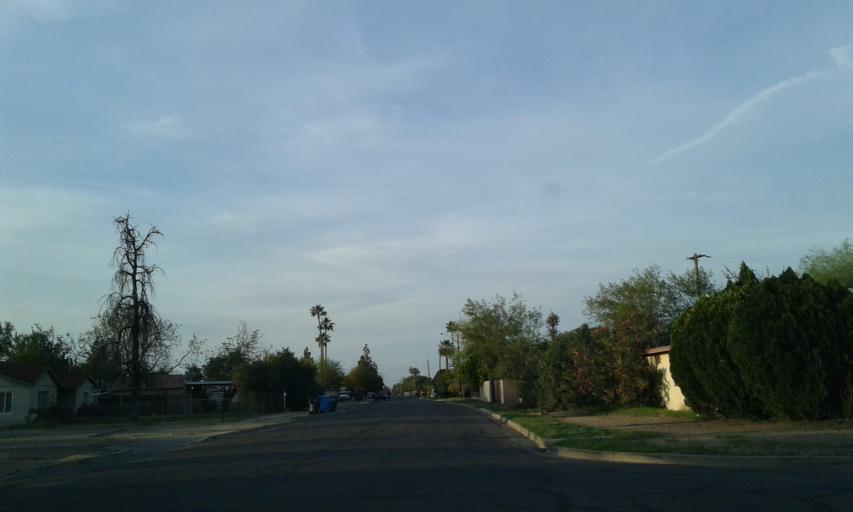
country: US
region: Arizona
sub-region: Maricopa County
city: Phoenix
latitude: 33.5104
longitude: -112.1042
